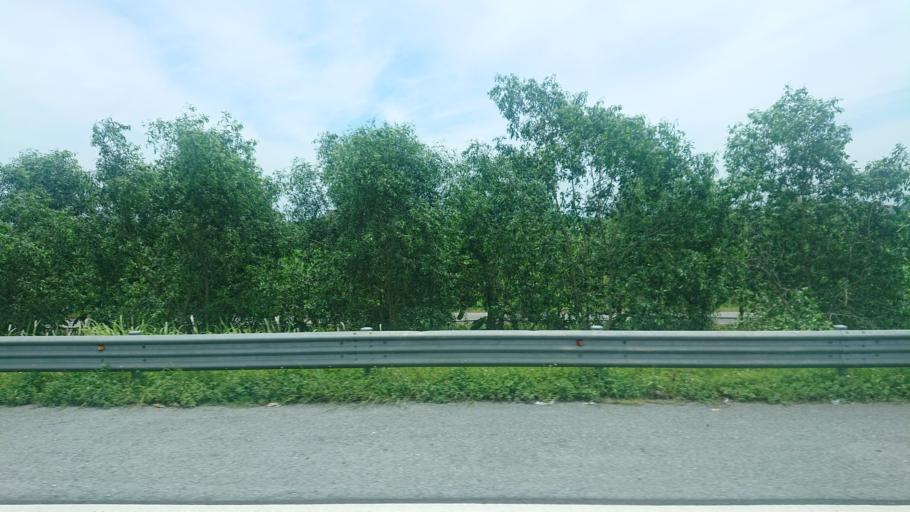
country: VN
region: Hai Phong
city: An Lao
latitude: 20.8126
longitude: 106.5005
